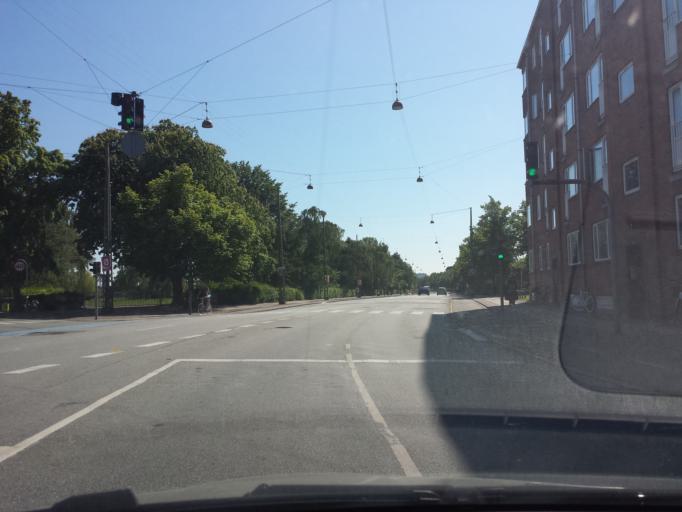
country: DK
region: Capital Region
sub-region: Kobenhavn
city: Christianshavn
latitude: 55.6530
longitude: 12.6023
